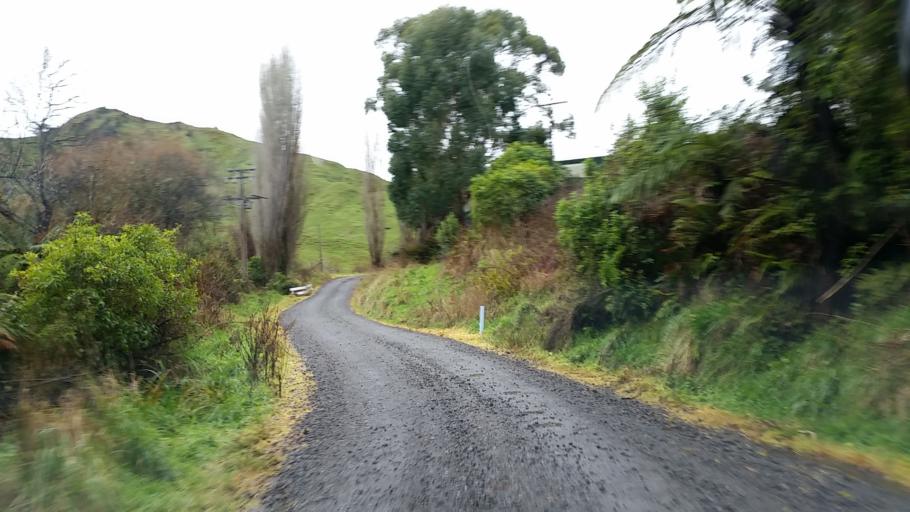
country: NZ
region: Taranaki
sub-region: South Taranaki District
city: Eltham
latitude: -39.5024
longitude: 174.4180
